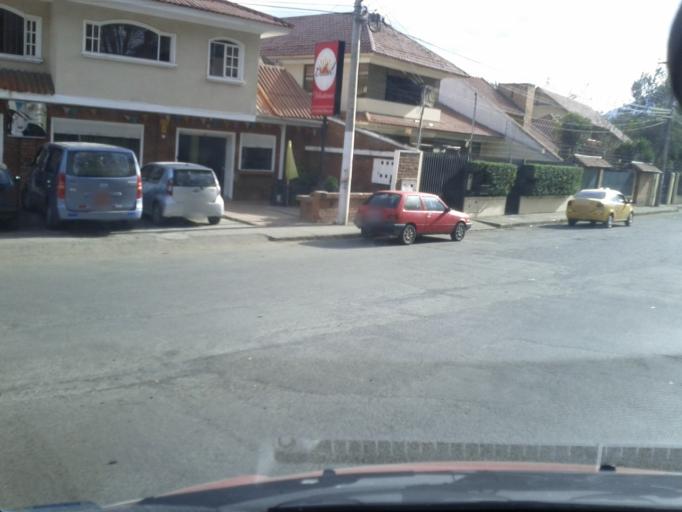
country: EC
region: Azuay
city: Cuenca
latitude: -2.8918
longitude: -79.0293
